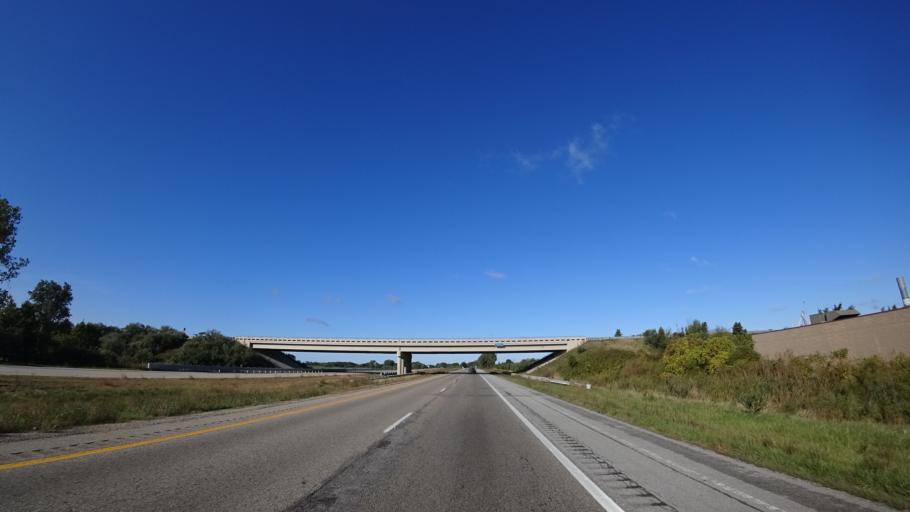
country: US
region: Michigan
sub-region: Ottawa County
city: Holland
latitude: 42.7367
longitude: -86.1144
